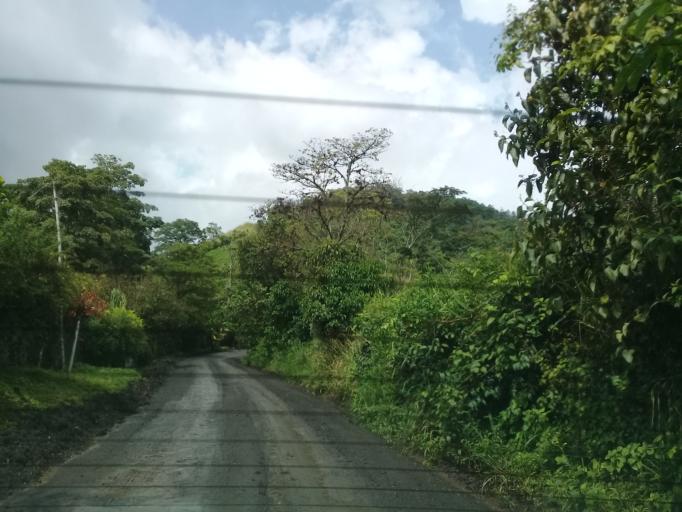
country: CO
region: Cundinamarca
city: Quipile
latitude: 4.6998
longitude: -74.5330
